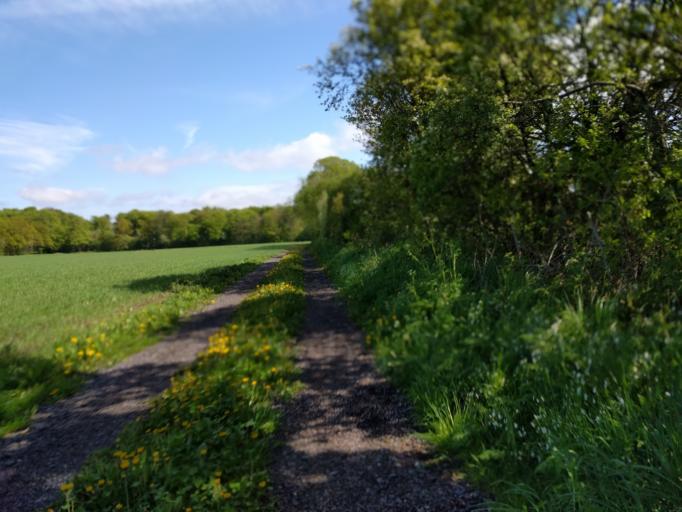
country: DK
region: South Denmark
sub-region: Kerteminde Kommune
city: Langeskov
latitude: 55.3871
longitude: 10.5748
